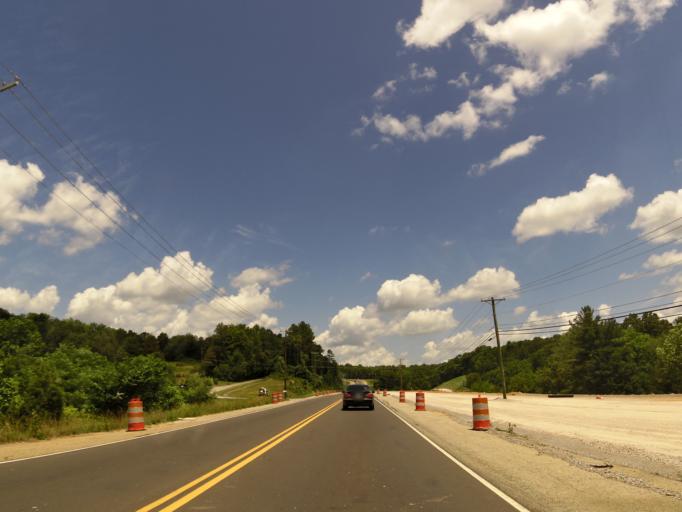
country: US
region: Tennessee
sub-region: Union County
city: Condon
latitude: 36.1287
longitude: -83.9145
